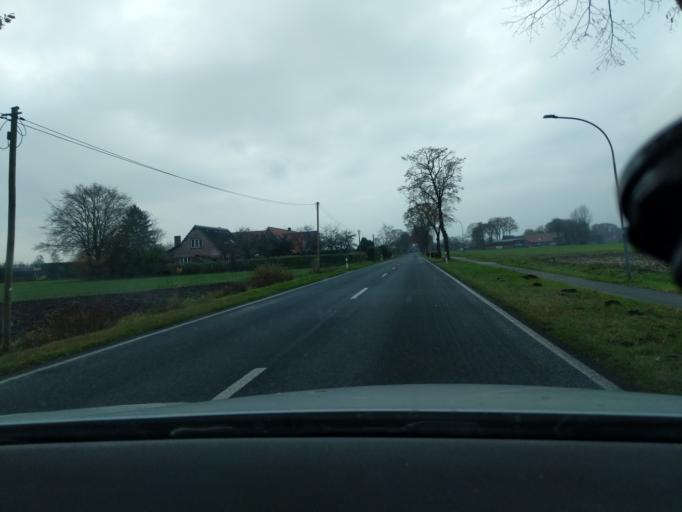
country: DE
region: Lower Saxony
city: Ahlerstedt
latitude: 53.3853
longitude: 9.4755
